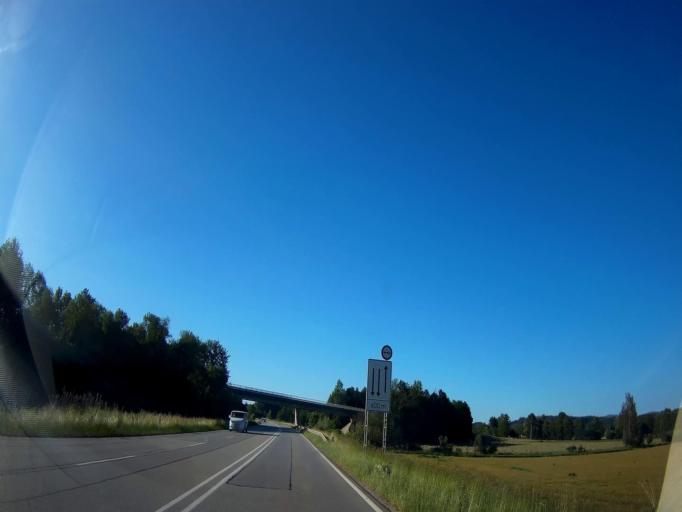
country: DE
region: Bavaria
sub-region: Lower Bavaria
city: Steinach
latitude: 48.9331
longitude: 12.6224
